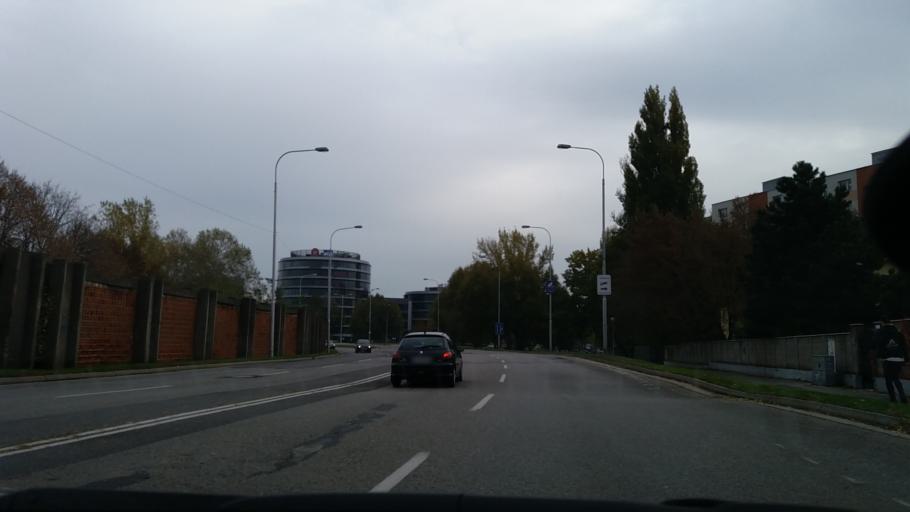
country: SK
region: Bratislavsky
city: Bratislava
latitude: 48.1252
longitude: 17.0969
